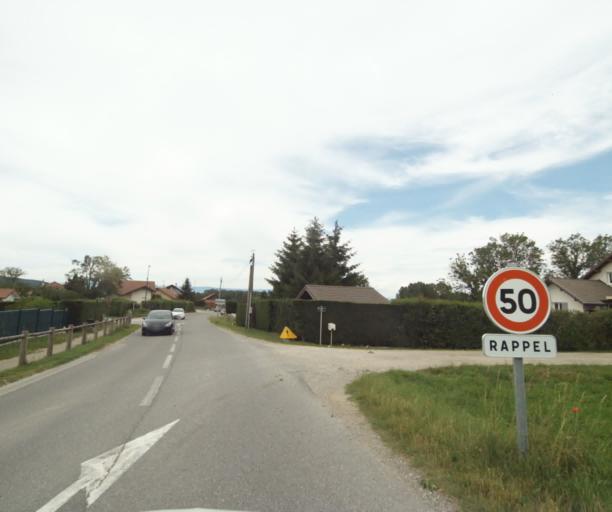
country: FR
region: Rhone-Alpes
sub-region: Departement de la Haute-Savoie
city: Perrignier
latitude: 46.2894
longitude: 6.4152
